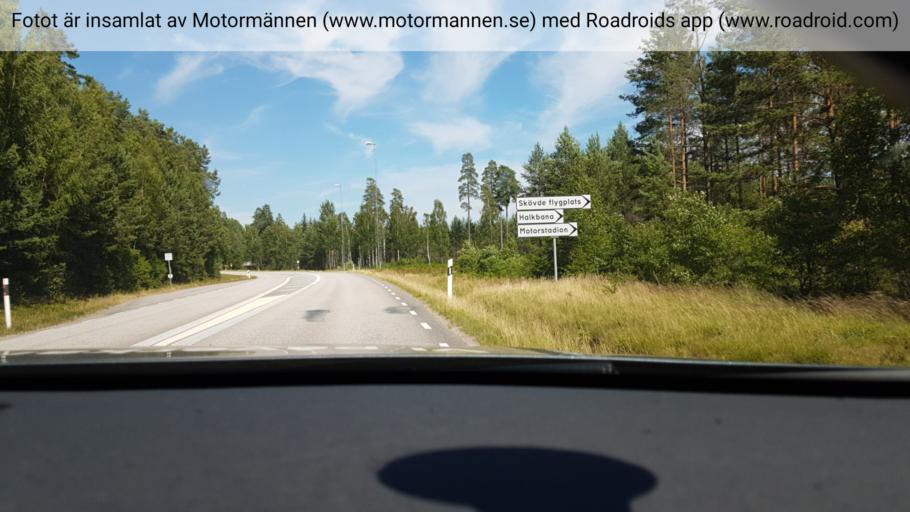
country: SE
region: Vaestra Goetaland
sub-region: Skovde Kommun
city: Stopen
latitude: 58.4517
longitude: 13.9519
